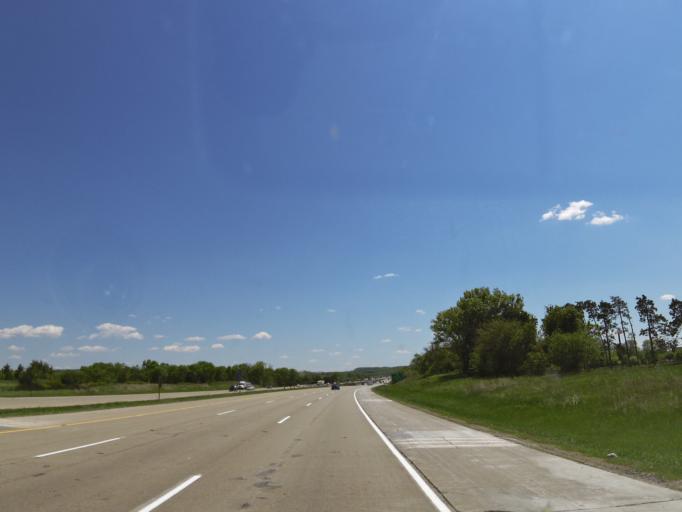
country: US
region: Wisconsin
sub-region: Columbia County
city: Poynette
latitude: 43.4091
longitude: -89.4677
